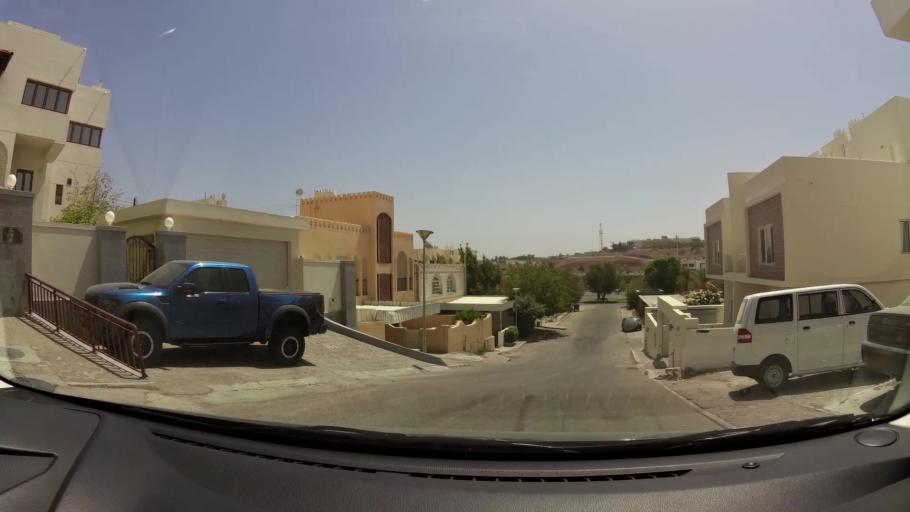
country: OM
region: Muhafazat Masqat
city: Bawshar
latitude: 23.5950
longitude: 58.4558
